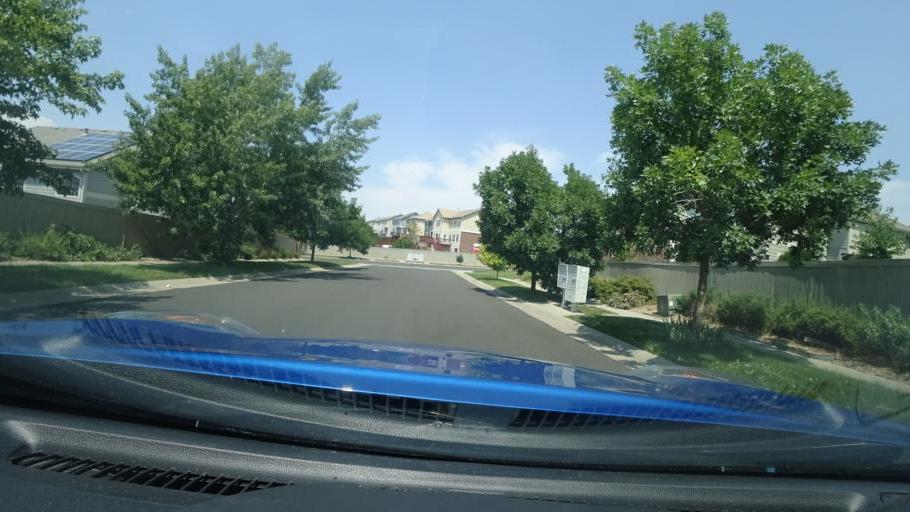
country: US
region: Colorado
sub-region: Adams County
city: Aurora
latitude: 39.6727
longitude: -104.7663
